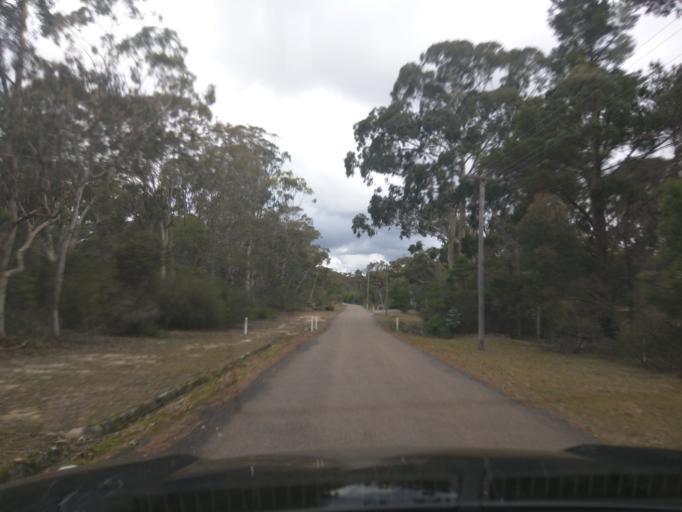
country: AU
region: New South Wales
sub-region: Wollongong
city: Mount Keira
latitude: -34.3281
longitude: 150.7456
